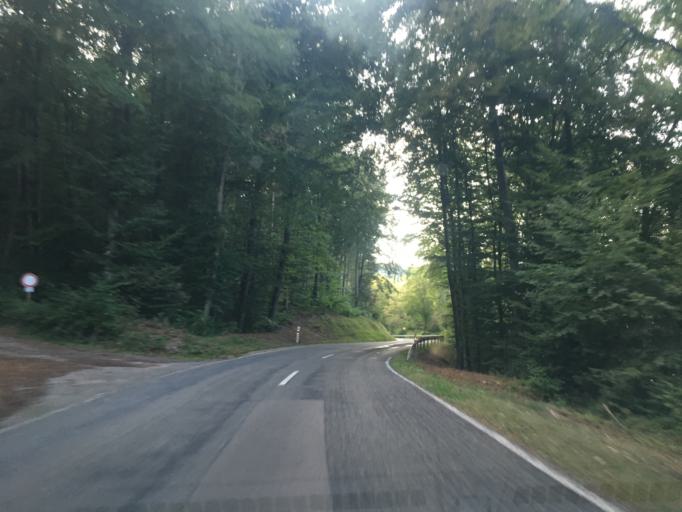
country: DE
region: Baden-Wuerttemberg
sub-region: Tuebingen Region
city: Rechtenstein
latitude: 48.2374
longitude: 9.5524
